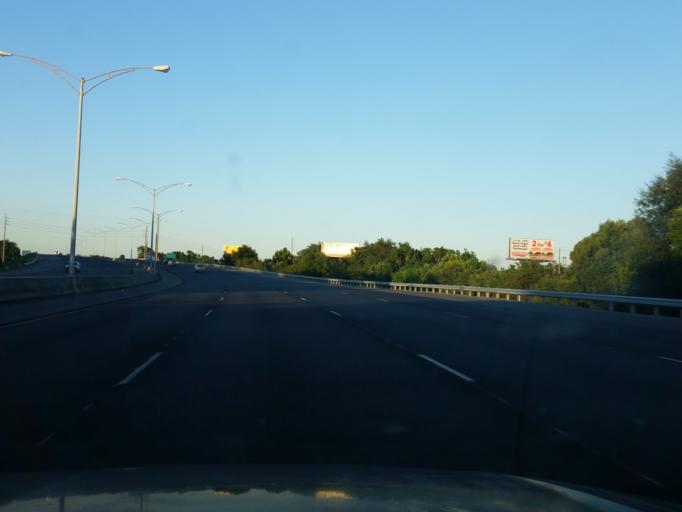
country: US
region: Alabama
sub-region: Mobile County
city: Mobile
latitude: 30.6649
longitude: -88.0521
